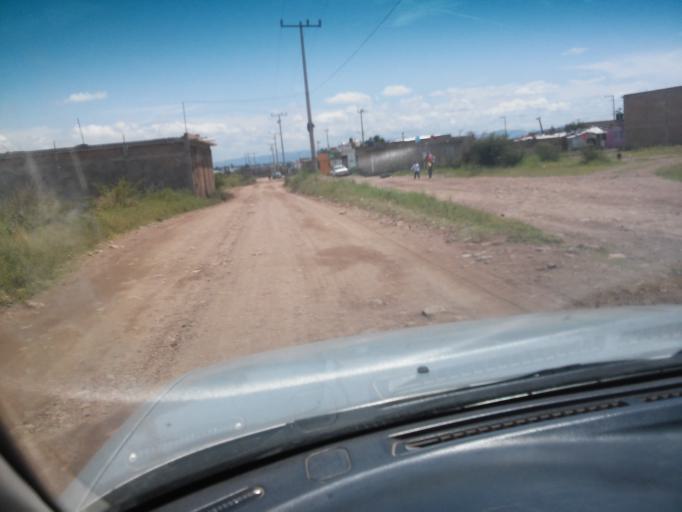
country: MX
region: Durango
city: Victoria de Durango
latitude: 23.9839
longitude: -104.7029
